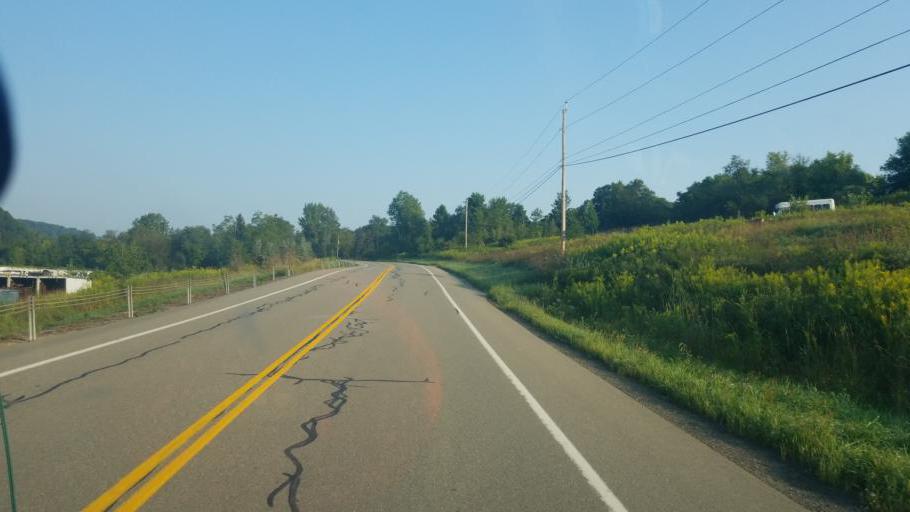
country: US
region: Pennsylvania
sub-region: Tioga County
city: Westfield
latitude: 42.0192
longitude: -77.5228
